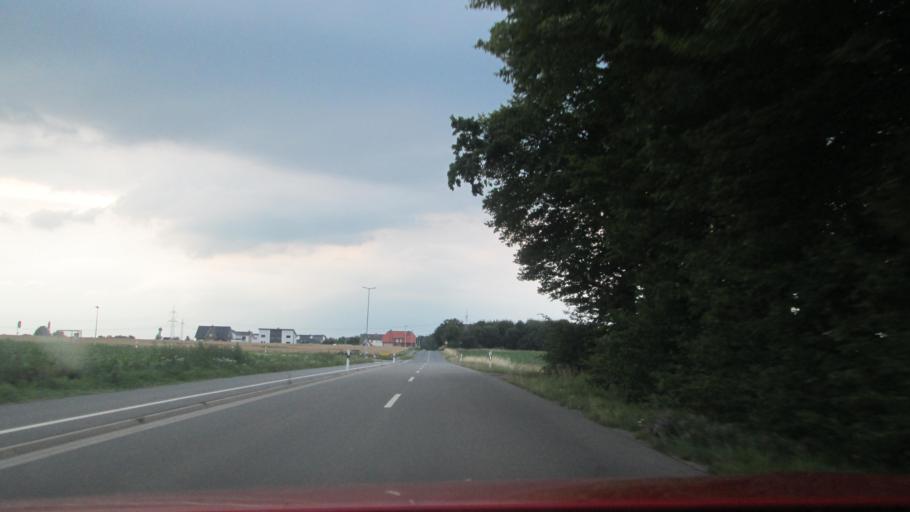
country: DE
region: Lower Saxony
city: Lehre
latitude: 52.3682
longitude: 10.6728
